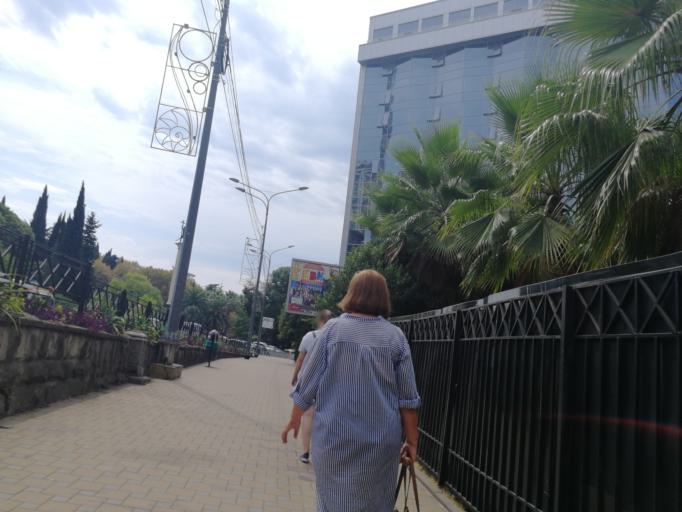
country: RU
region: Krasnodarskiy
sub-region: Sochi City
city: Sochi
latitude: 43.5836
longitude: 39.7230
